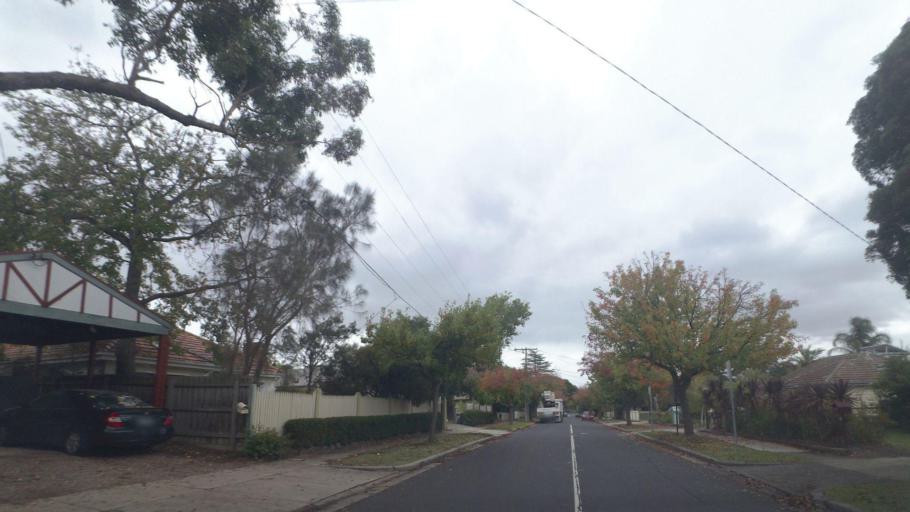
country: AU
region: Victoria
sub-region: Whitehorse
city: Nunawading
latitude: -37.8255
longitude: 145.1768
